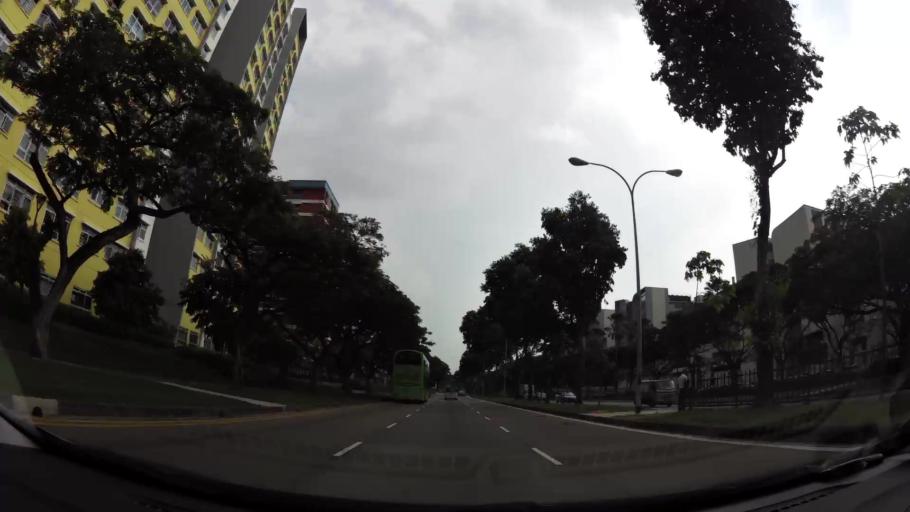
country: SG
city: Singapore
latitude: 1.3465
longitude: 103.9338
